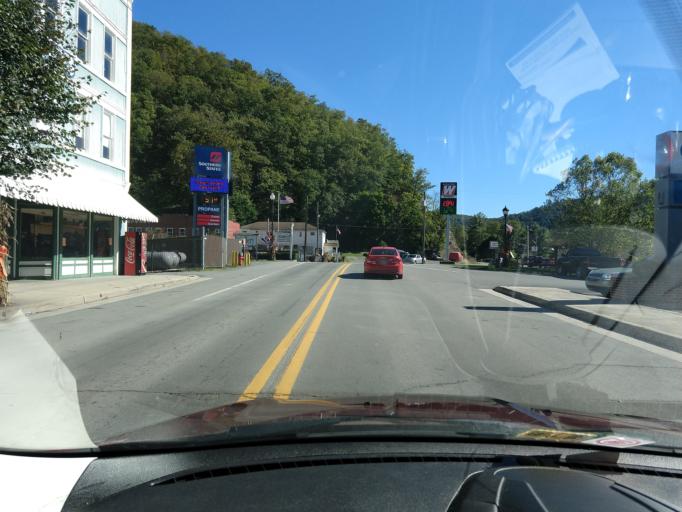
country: US
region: West Virginia
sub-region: Pocahontas County
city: Marlinton
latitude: 38.2228
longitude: -80.0934
